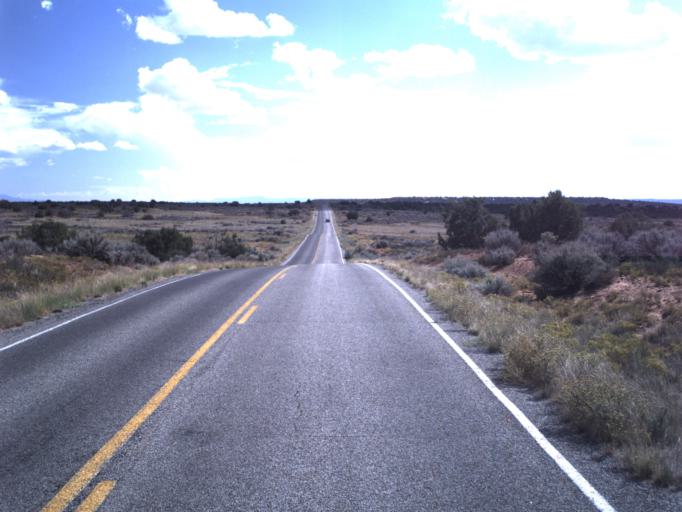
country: US
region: Utah
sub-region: Grand County
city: Moab
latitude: 38.5107
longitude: -109.7294
